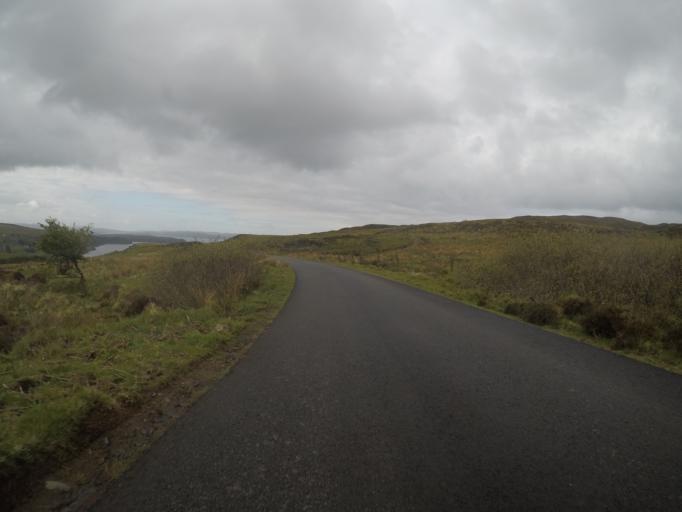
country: GB
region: Scotland
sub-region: Highland
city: Portree
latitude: 57.5982
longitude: -6.3556
